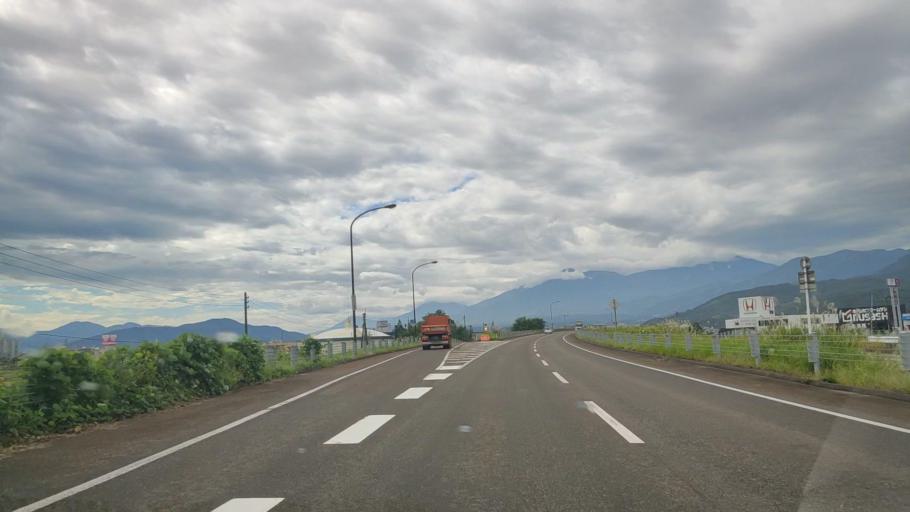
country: JP
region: Niigata
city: Arai
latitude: 37.0617
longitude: 138.2615
